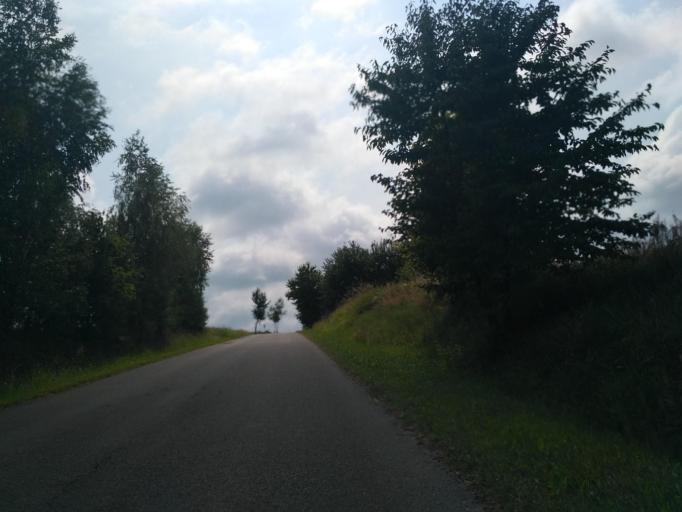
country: PL
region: Subcarpathian Voivodeship
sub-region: Powiat rzeszowski
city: Chmielnik
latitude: 50.0070
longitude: 22.1497
